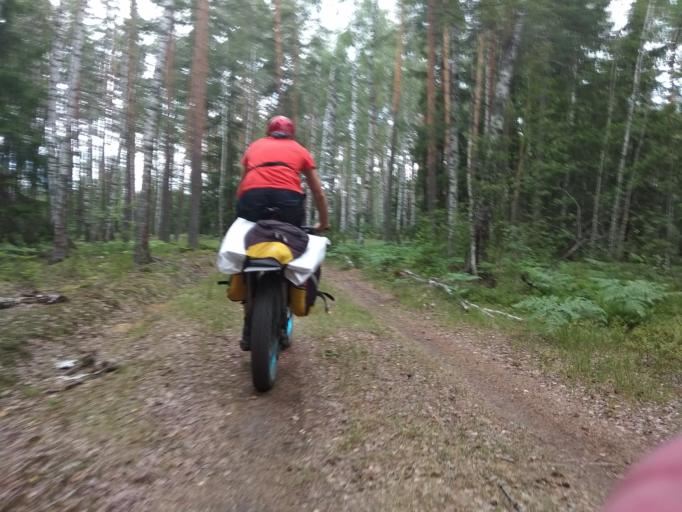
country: RU
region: Moskovskaya
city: Misheronskiy
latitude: 55.6352
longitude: 39.7335
